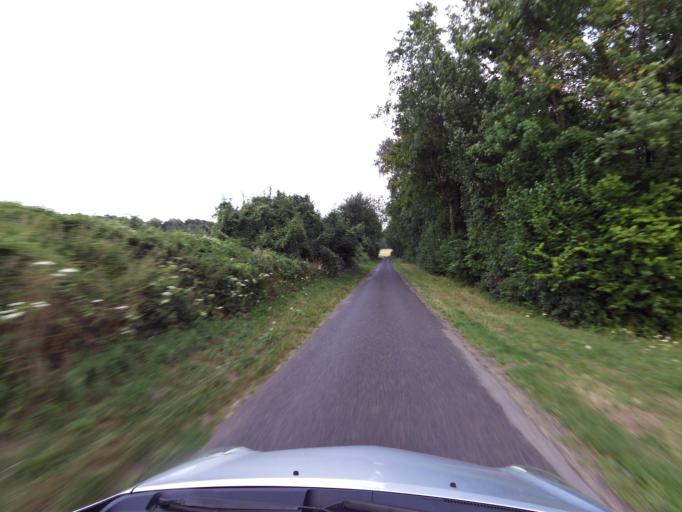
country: FR
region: Picardie
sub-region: Departement de l'Aisne
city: Bruyeres-et-Montberault
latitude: 49.4979
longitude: 3.6367
